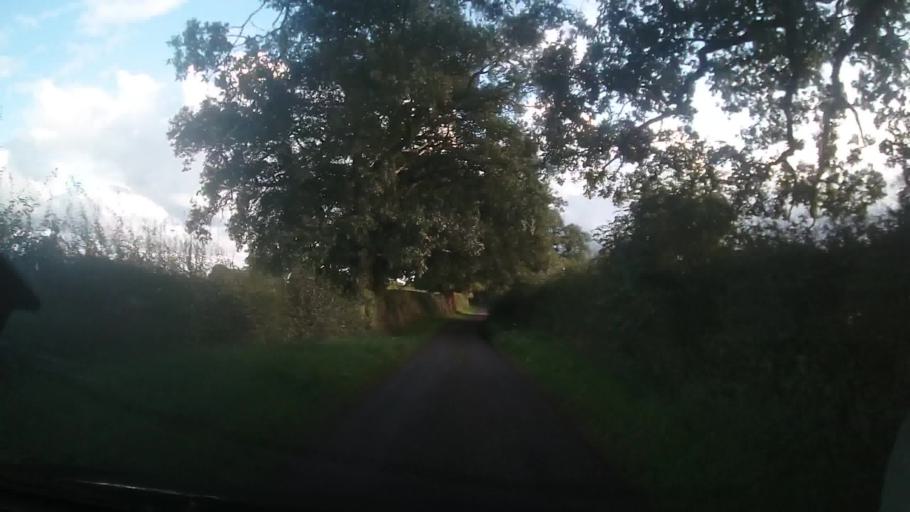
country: GB
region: England
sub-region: Shropshire
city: Wem
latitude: 52.8798
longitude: -2.7302
